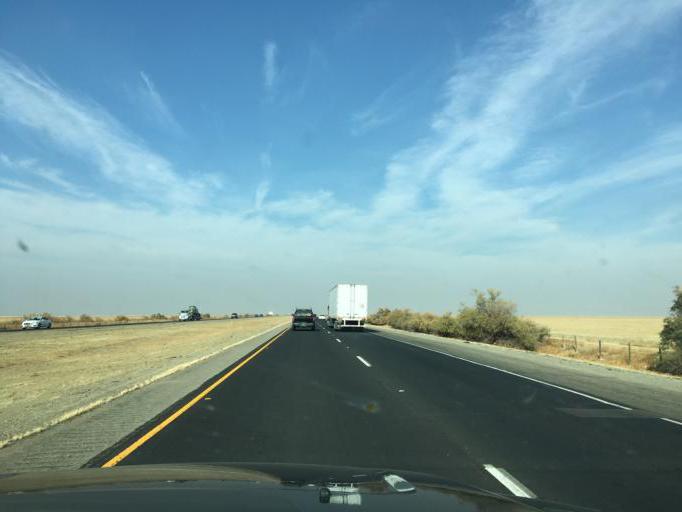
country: US
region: California
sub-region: Kern County
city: Lost Hills
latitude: 35.7408
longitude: -119.7458
